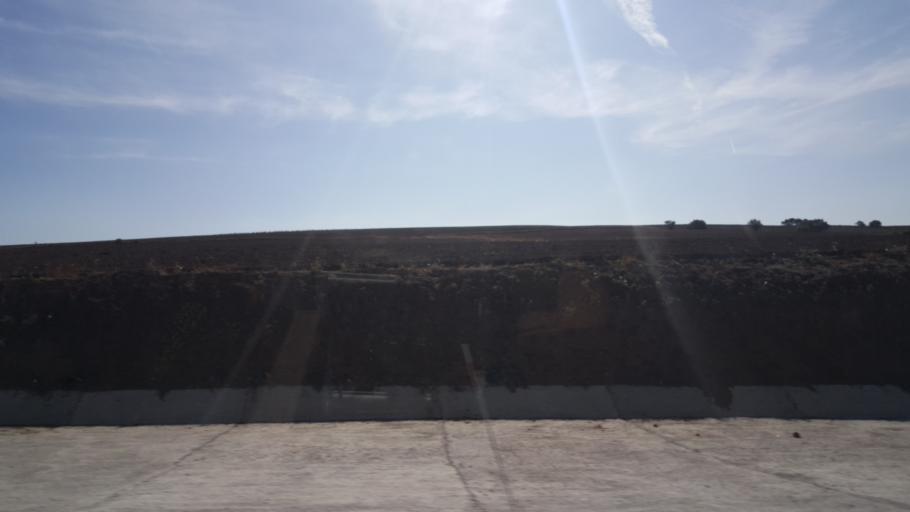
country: TR
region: Ankara
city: Haymana
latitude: 39.4016
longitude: 32.6224
